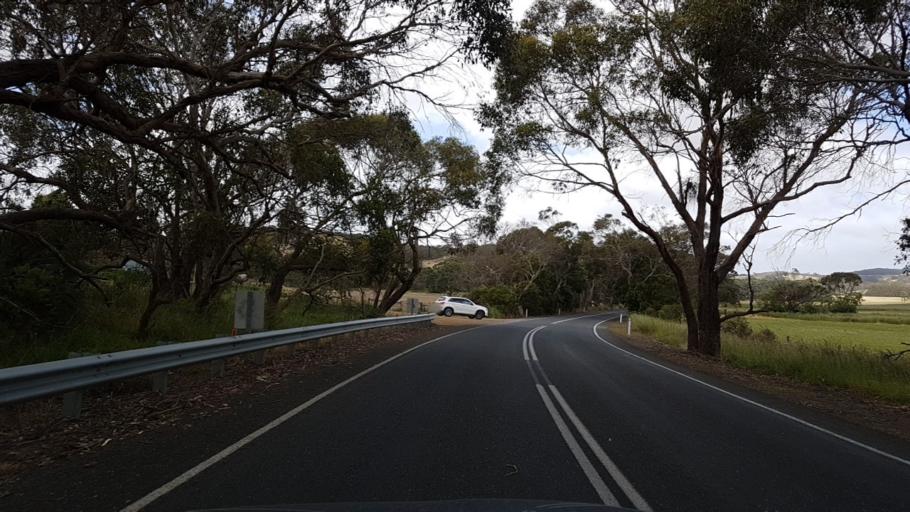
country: AU
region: South Australia
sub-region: Alexandrina
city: Mount Compass
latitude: -35.4087
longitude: 138.5375
